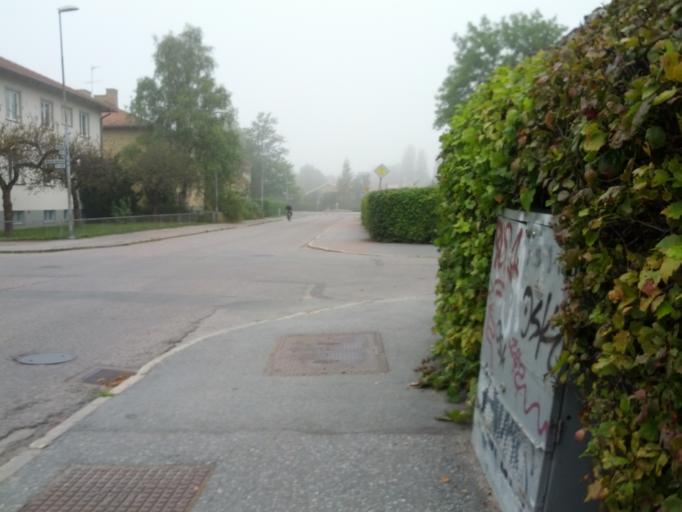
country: SE
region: Uppsala
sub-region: Uppsala Kommun
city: Uppsala
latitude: 59.8452
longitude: 17.6318
